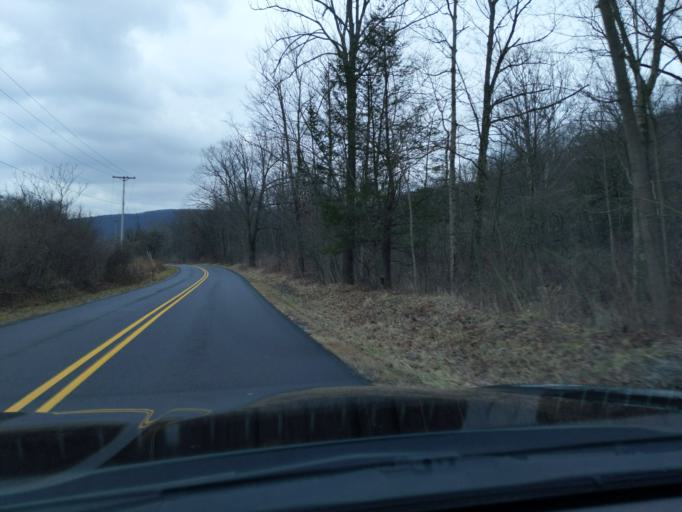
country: US
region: Pennsylvania
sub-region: Blair County
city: Tipton
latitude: 40.6278
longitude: -78.3104
